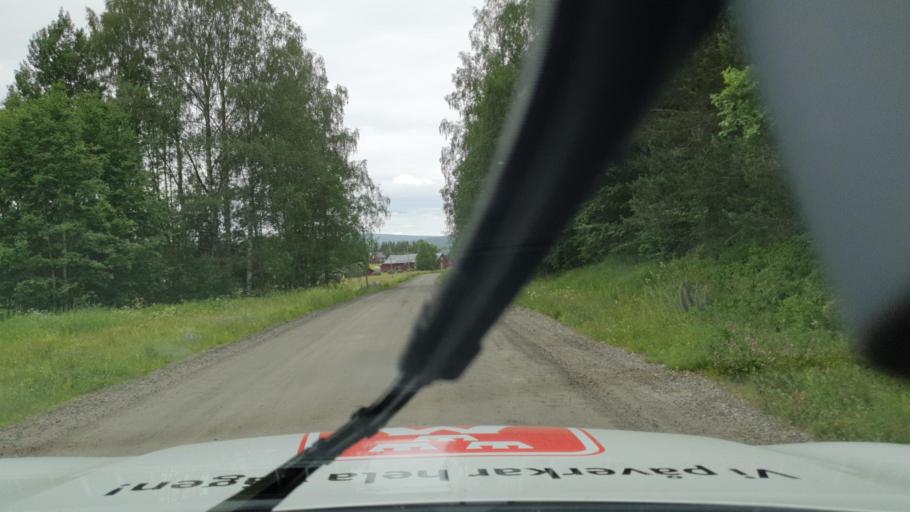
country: SE
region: Vaesterbotten
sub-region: Bjurholms Kommun
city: Bjurholm
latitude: 63.7804
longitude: 19.3862
